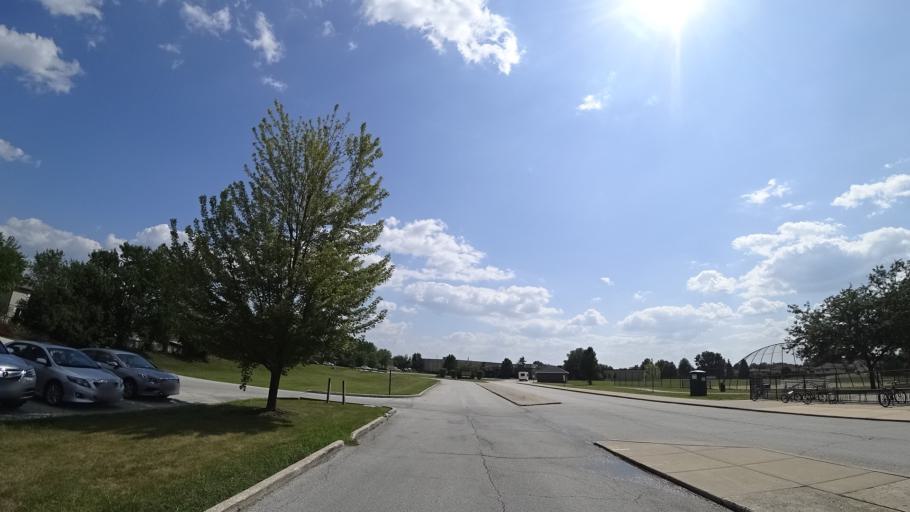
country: US
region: Illinois
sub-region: Cook County
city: Orland Park
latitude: 41.6153
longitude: -87.8343
